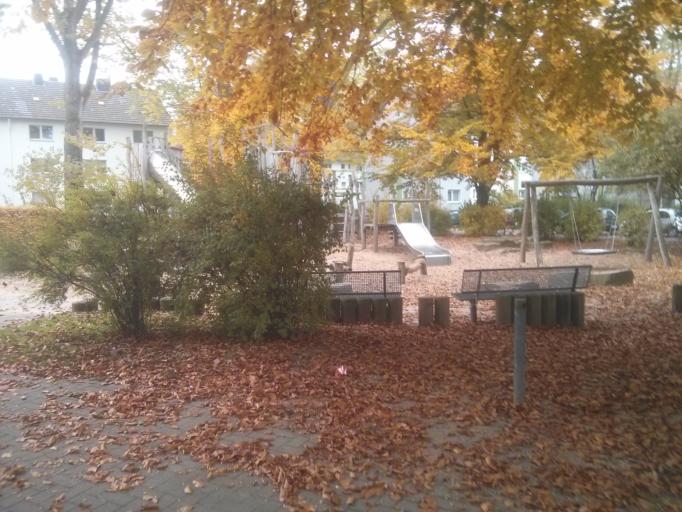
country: DE
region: North Rhine-Westphalia
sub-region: Regierungsbezirk Koln
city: Porz am Rhein
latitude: 50.9001
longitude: 7.0275
